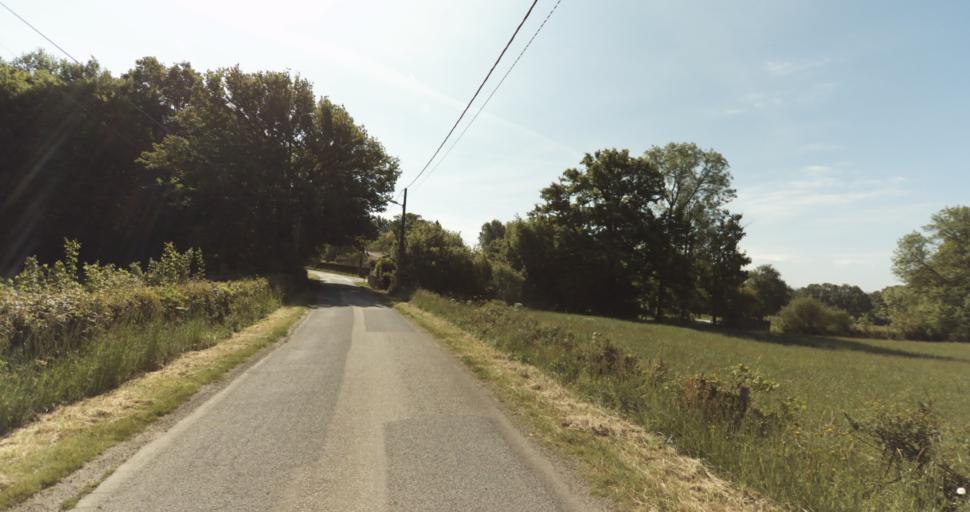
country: FR
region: Limousin
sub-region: Departement de la Haute-Vienne
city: Le Vigen
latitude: 45.7195
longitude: 1.2742
